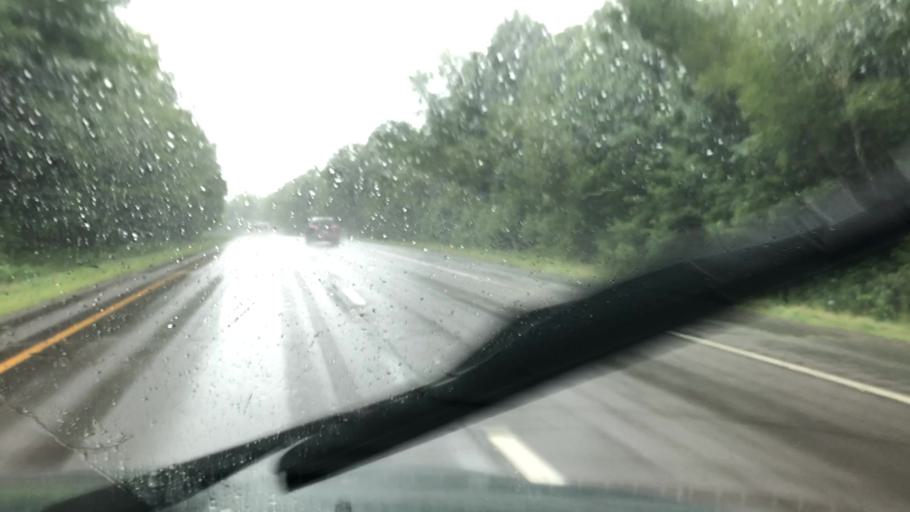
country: US
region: Pennsylvania
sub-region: Pike County
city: Gold Key Lake
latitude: 41.3471
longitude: -74.9309
